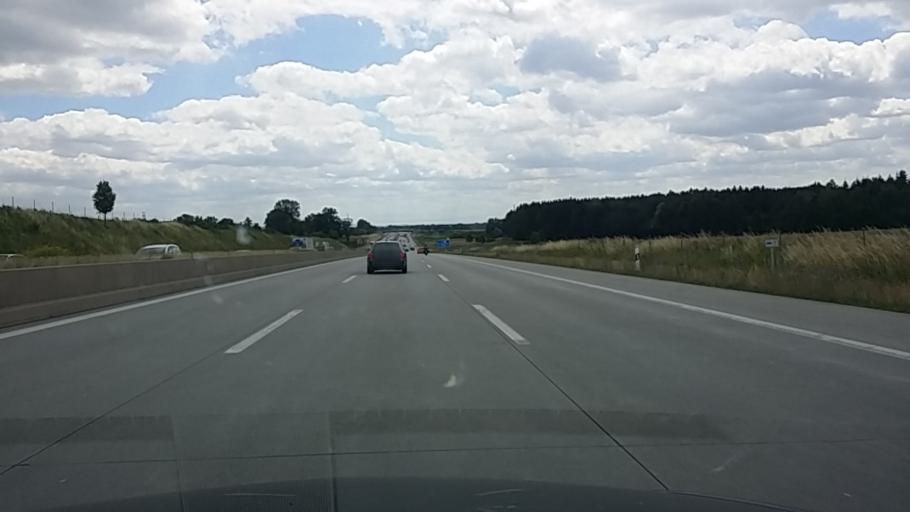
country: DE
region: Bavaria
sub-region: Upper Bavaria
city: Sulzemoos
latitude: 48.2687
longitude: 11.2892
